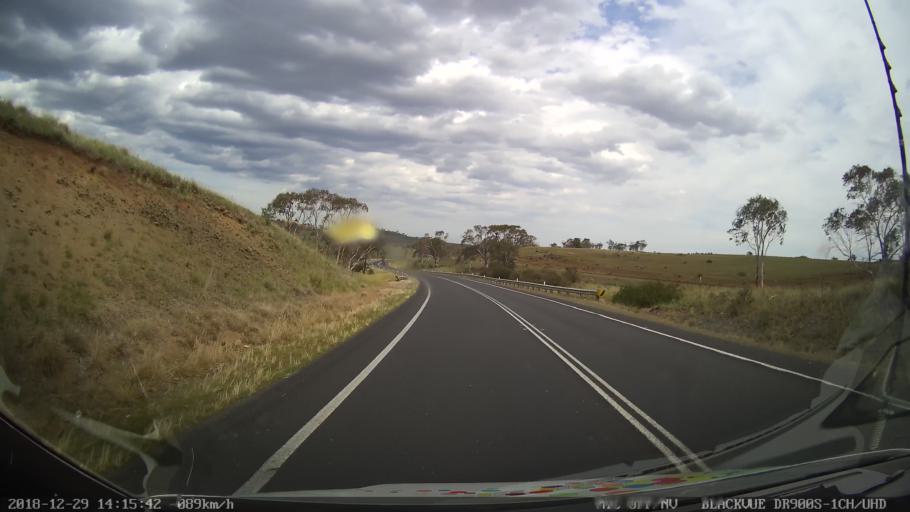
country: AU
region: New South Wales
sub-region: Cooma-Monaro
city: Cooma
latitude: -36.4590
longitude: 149.2429
